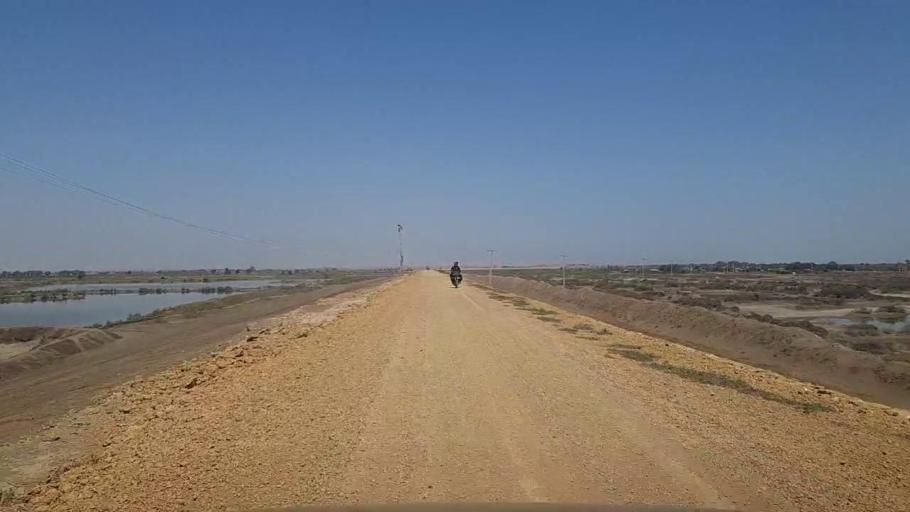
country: PK
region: Sindh
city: Thatta
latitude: 24.7868
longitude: 67.9966
